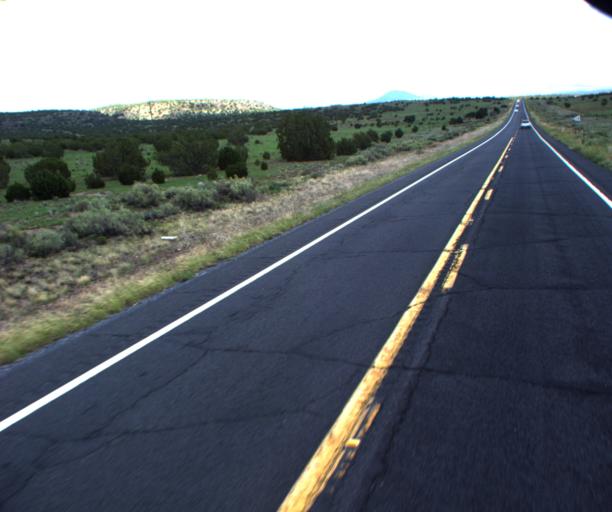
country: US
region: Arizona
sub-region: Coconino County
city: Williams
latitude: 35.4986
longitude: -112.1741
